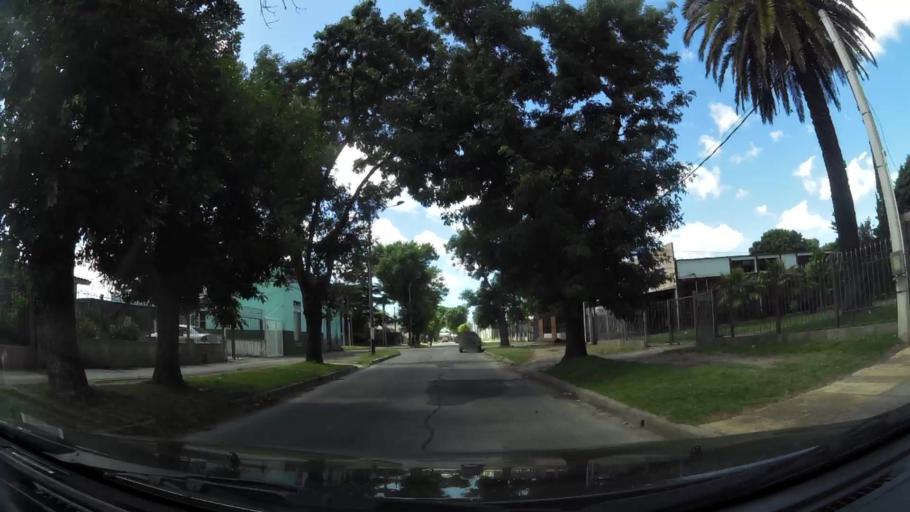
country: UY
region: Canelones
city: Paso de Carrasco
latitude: -34.8387
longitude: -56.1238
